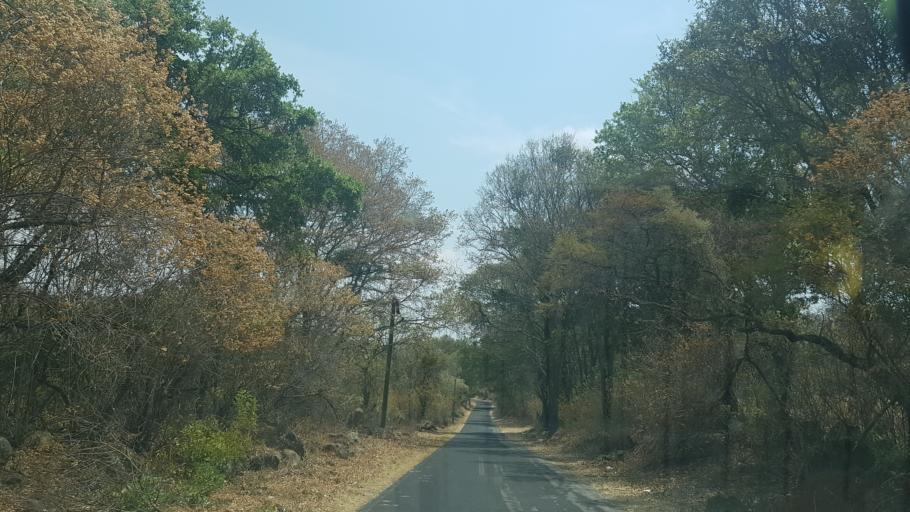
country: MX
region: Puebla
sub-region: Tochimilco
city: La Magdalena Yancuitlalpan
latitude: 18.8864
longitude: -98.5958
